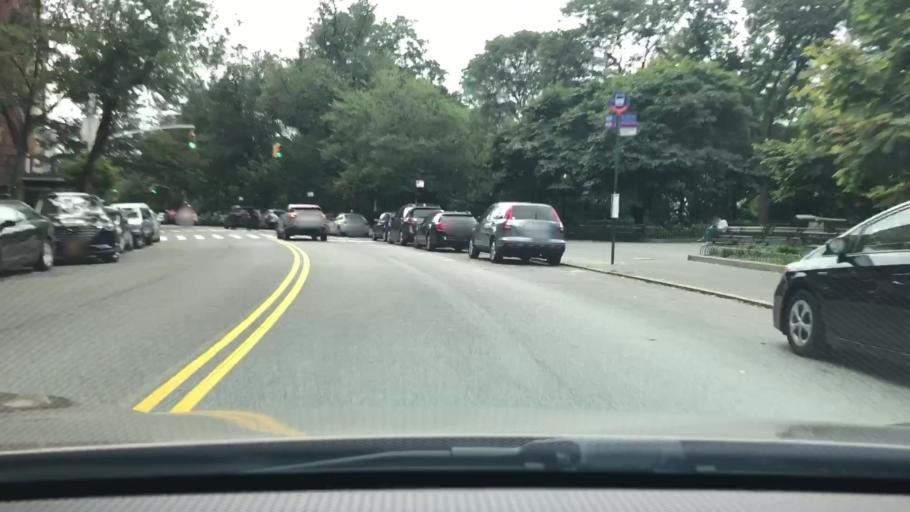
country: US
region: New York
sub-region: New York County
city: Manhattan
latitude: 40.7916
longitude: -73.9790
